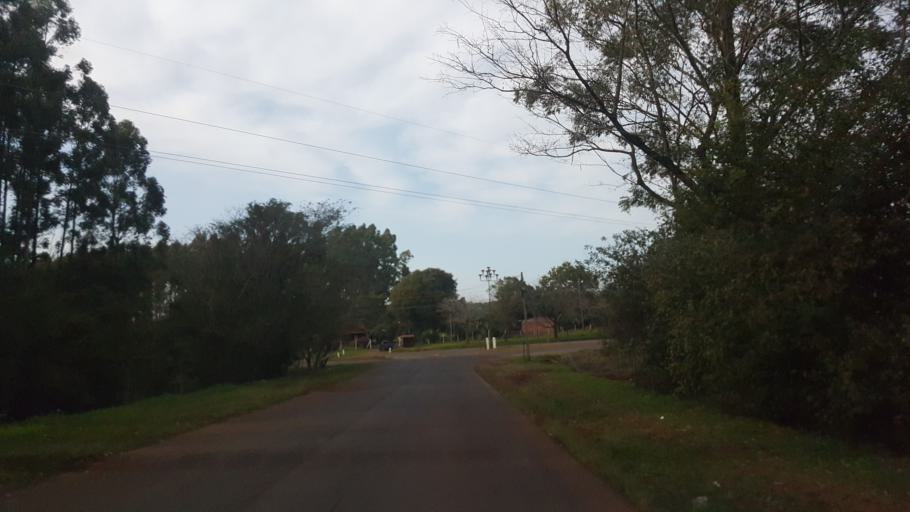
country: AR
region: Misiones
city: Capiovi
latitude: -26.9395
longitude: -55.0802
